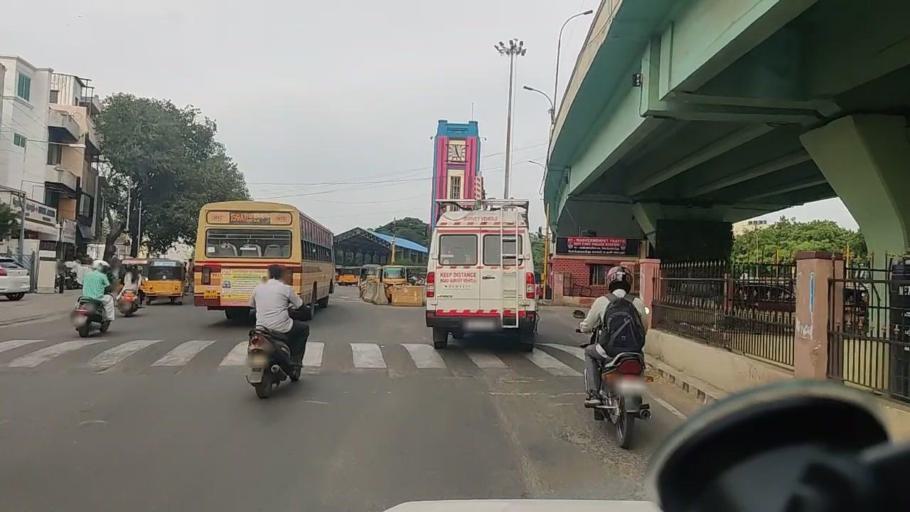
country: IN
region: Tamil Nadu
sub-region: Chennai
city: George Town
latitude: 13.1056
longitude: 80.2793
